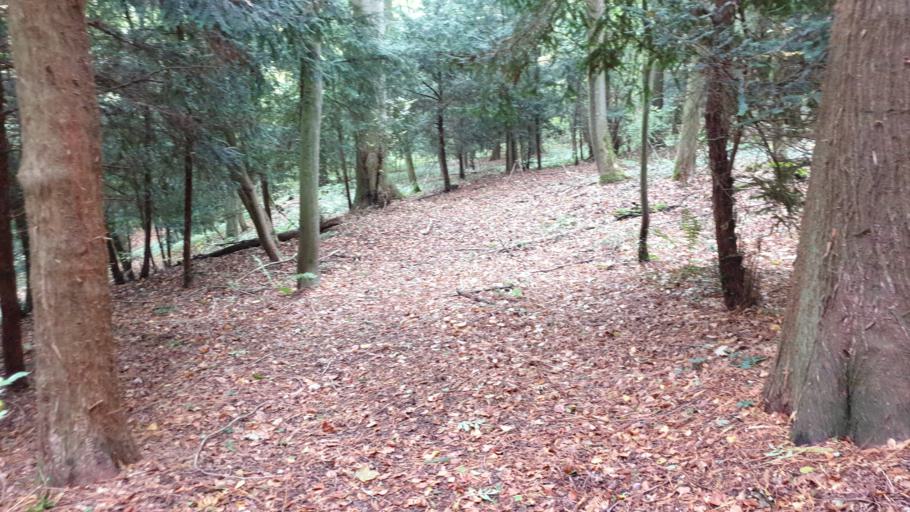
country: DE
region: Brandenburg
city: Chorin
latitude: 52.8911
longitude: 13.8834
